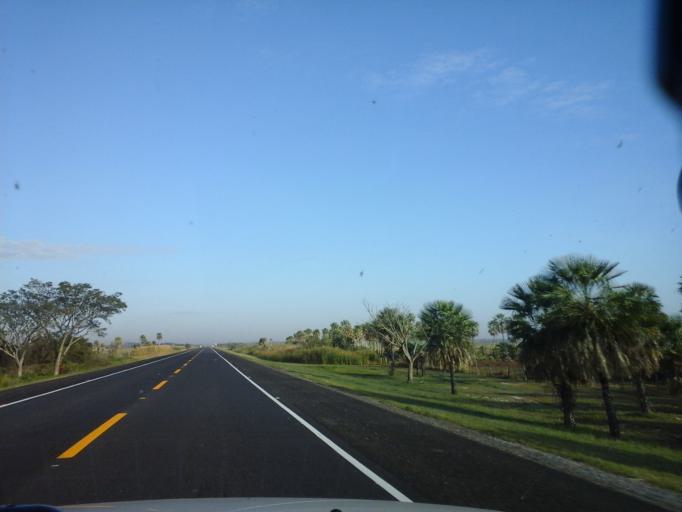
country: PY
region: Neembucu
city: Pilar
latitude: -26.8652
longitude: -57.8295
